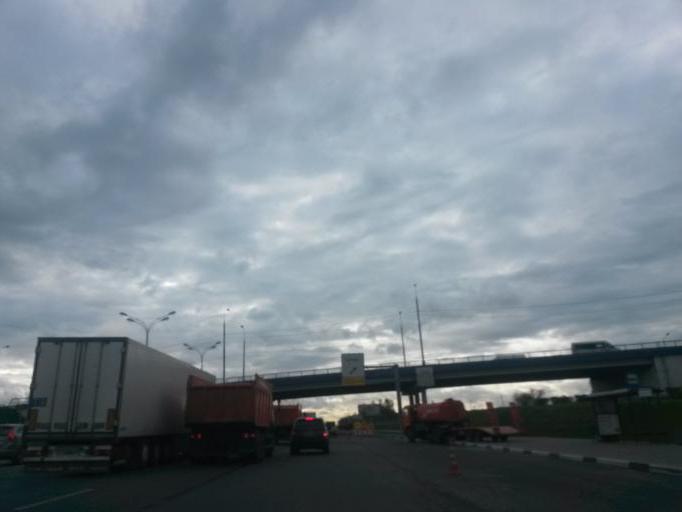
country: RU
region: Moscow
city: Chertanovo Yuzhnoye
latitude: 55.5808
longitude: 37.5745
